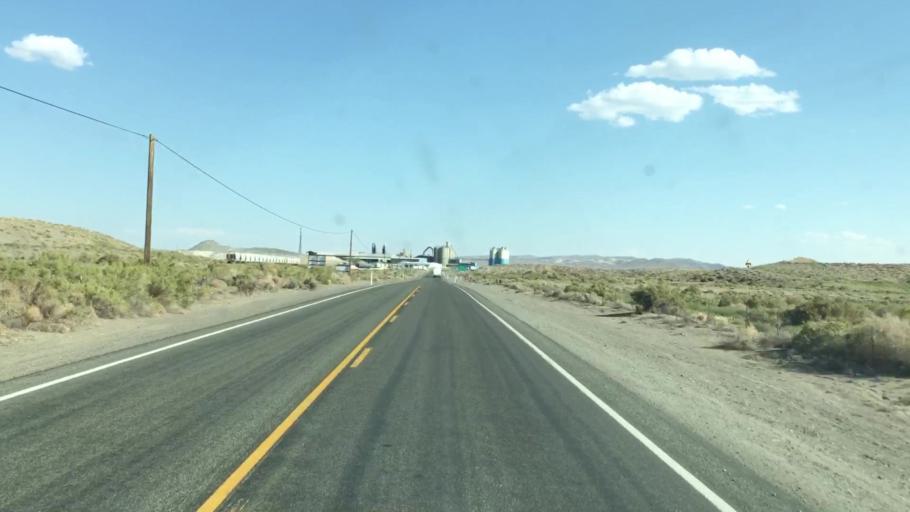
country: US
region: Nevada
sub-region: Lyon County
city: Fernley
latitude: 39.6282
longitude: -119.2744
